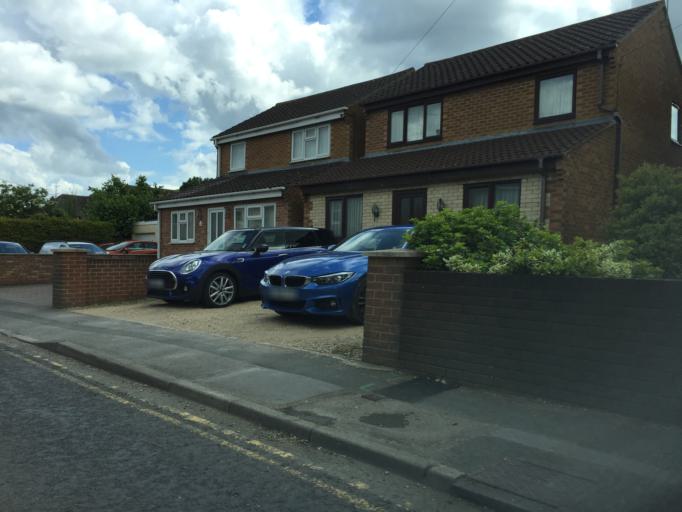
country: GB
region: England
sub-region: Borough of Swindon
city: Broad Blunsdon
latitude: 51.5860
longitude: -1.7521
